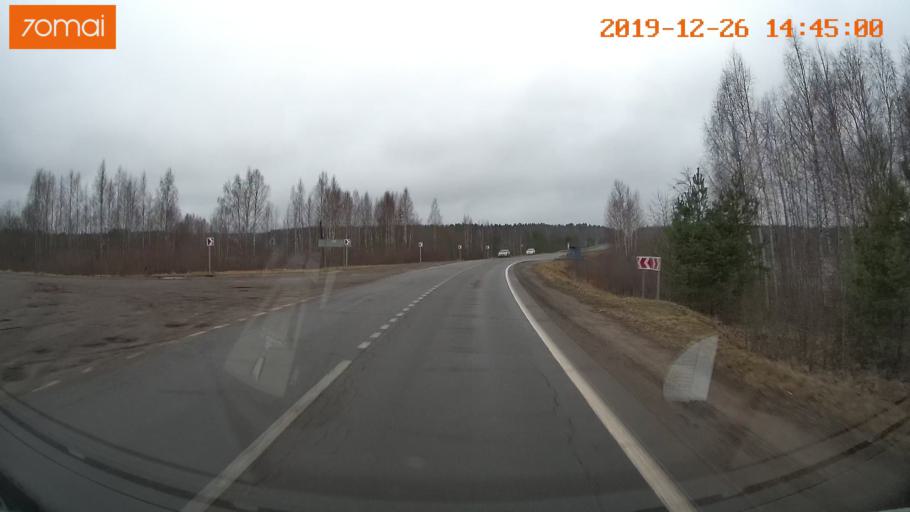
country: RU
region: Jaroslavl
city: Poshekhon'ye
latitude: 58.3411
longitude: 39.0486
